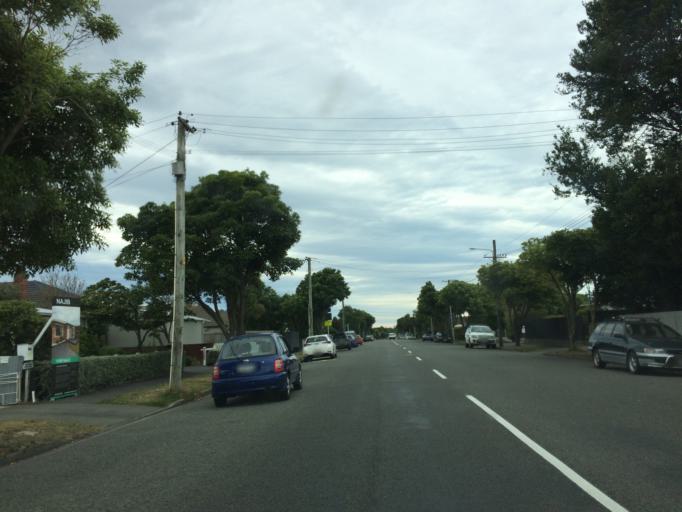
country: NZ
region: Canterbury
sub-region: Selwyn District
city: Prebbleton
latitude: -43.5198
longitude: 172.5440
